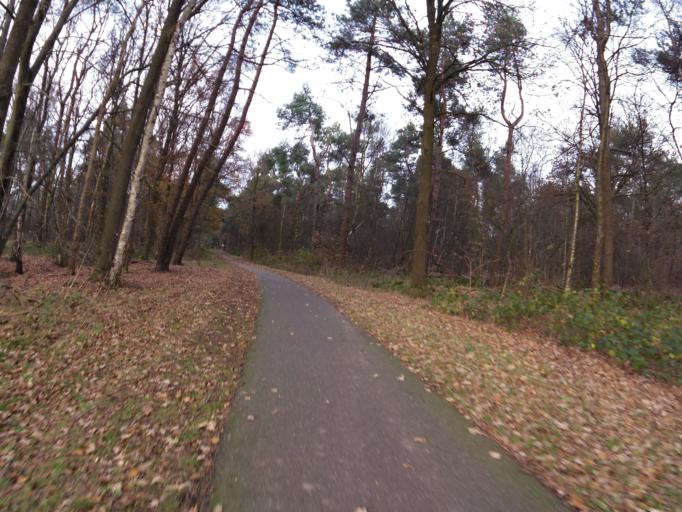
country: NL
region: North Brabant
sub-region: Gemeente Oss
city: Berghem
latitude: 51.7249
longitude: 5.5776
